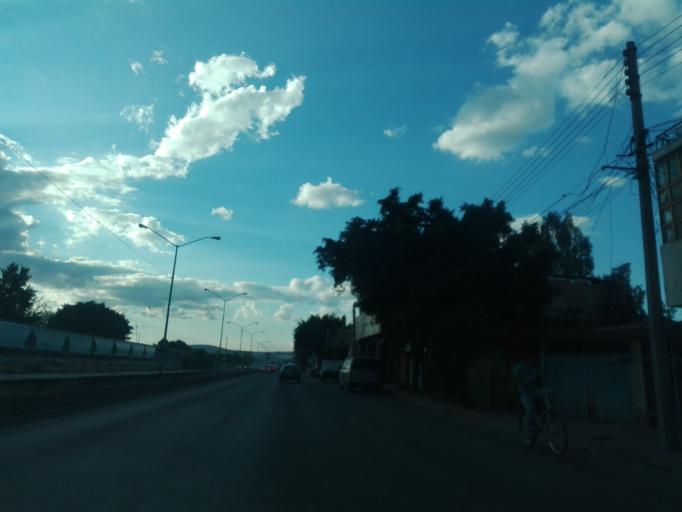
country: MX
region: Guanajuato
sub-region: Leon
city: San Jose de Duran (Los Troncoso)
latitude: 21.0854
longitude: -101.6677
